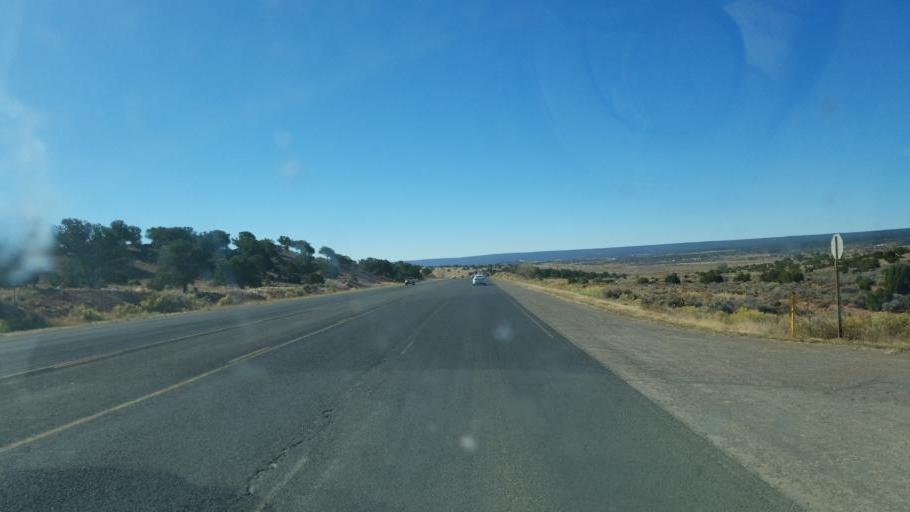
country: US
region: Arizona
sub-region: Apache County
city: Fort Defiance
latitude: 35.7188
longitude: -109.0585
